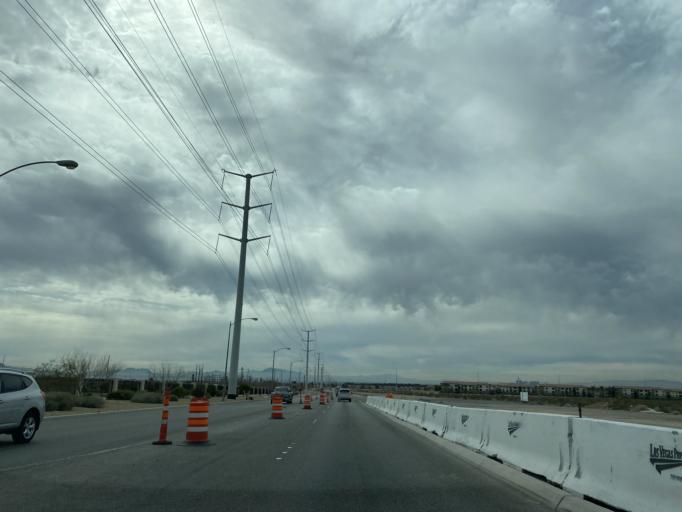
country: US
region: Nevada
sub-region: Clark County
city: Nellis Air Force Base
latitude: 36.2850
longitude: -115.0987
